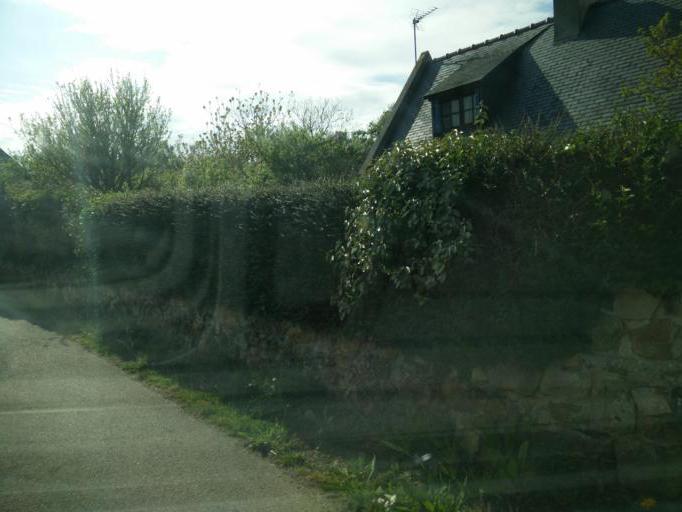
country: FR
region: Brittany
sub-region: Departement du Finistere
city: Crozon
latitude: 48.2346
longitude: -4.5473
